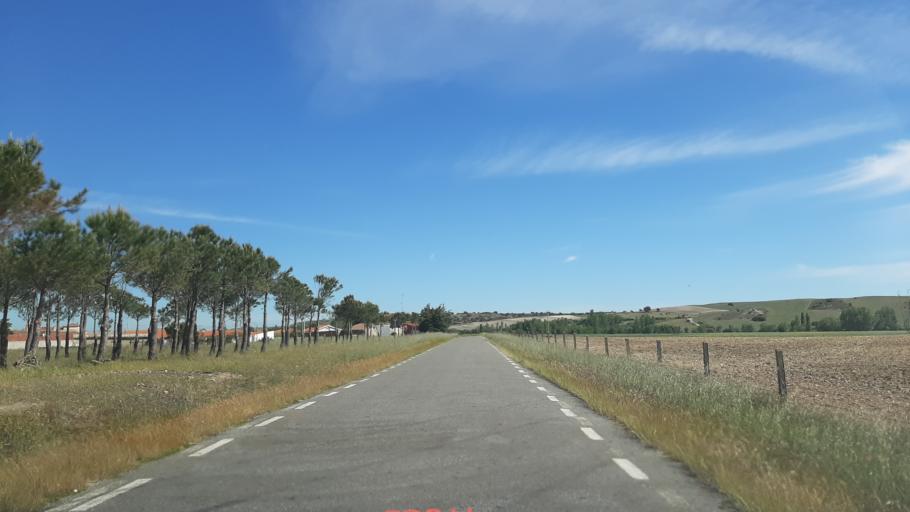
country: ES
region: Castille and Leon
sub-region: Provincia de Salamanca
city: Pedrosillo de Alba
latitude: 40.8065
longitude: -5.3806
